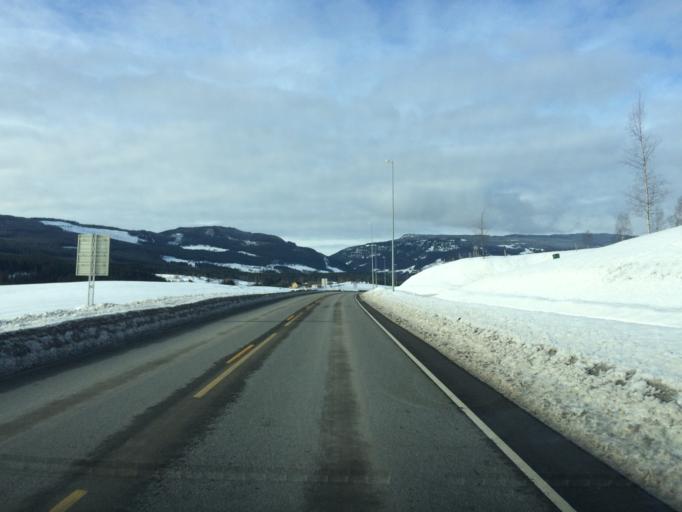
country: NO
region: Oppland
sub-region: Gausdal
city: Segalstad bru
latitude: 61.2200
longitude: 10.2588
